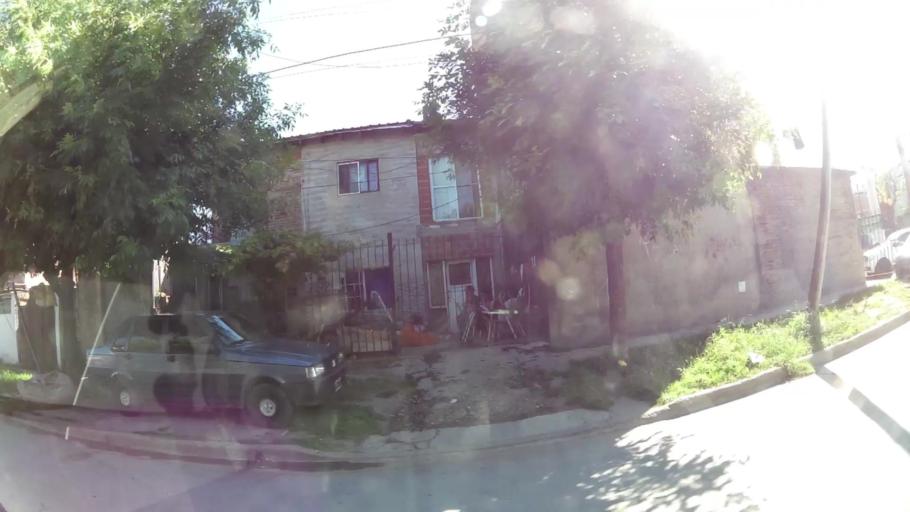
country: AR
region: Buenos Aires
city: Hurlingham
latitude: -34.5441
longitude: -58.5942
